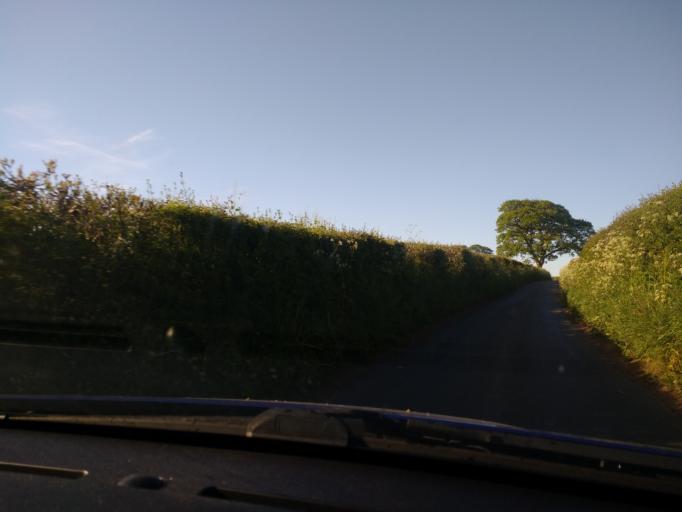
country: GB
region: England
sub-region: Cumbria
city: Appleby-in-Westmorland
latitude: 54.6757
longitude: -2.5903
